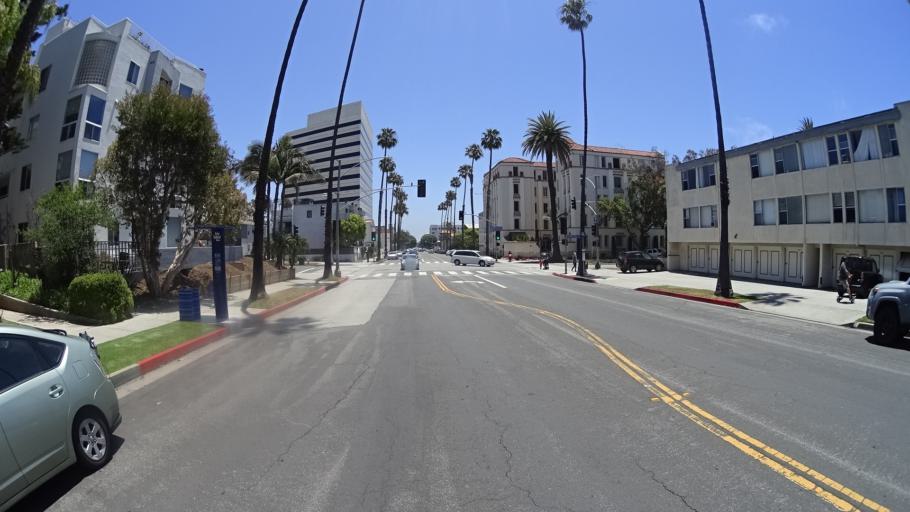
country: US
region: California
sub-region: Los Angeles County
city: Santa Monica
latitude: 34.0208
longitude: -118.5002
